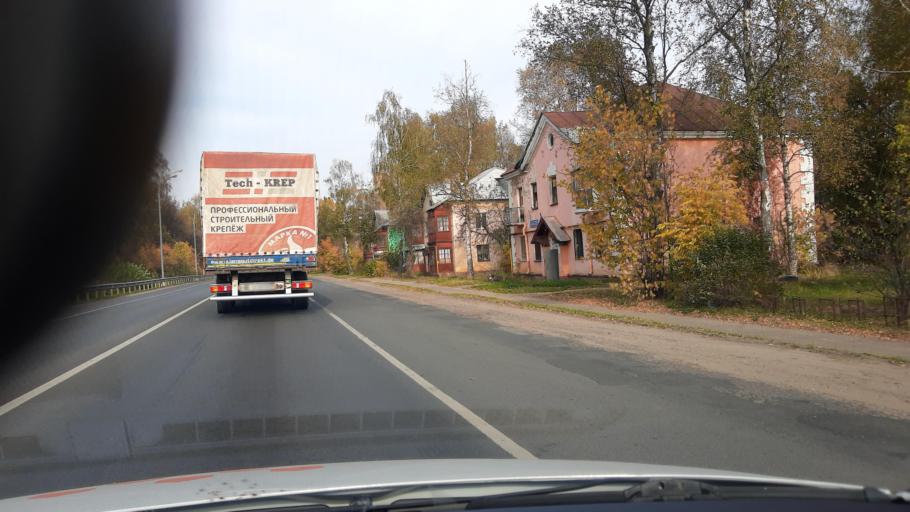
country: RU
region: Moskovskaya
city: Elektrostal'
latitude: 55.7936
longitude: 38.4301
